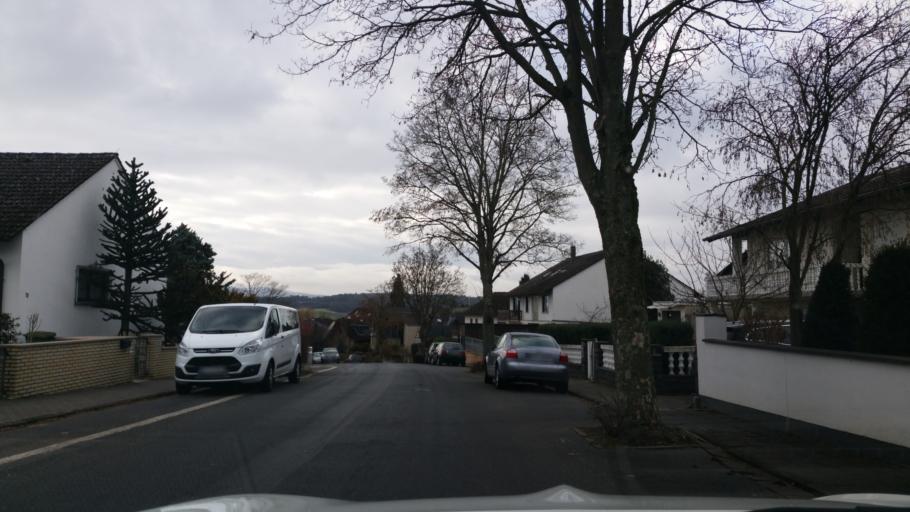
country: DE
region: Hesse
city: Reinheim
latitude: 49.8314
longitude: 8.8239
